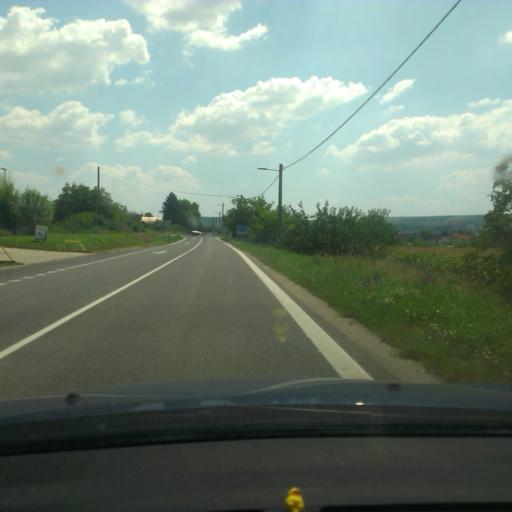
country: SK
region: Trnavsky
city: Hlohovec
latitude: 48.4468
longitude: 17.8108
